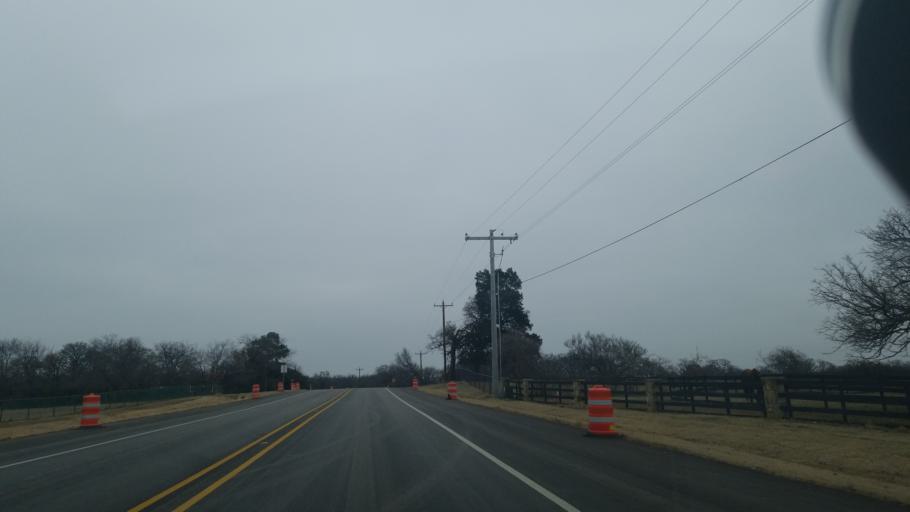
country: US
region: Texas
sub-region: Denton County
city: Argyle
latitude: 33.1264
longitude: -97.1395
